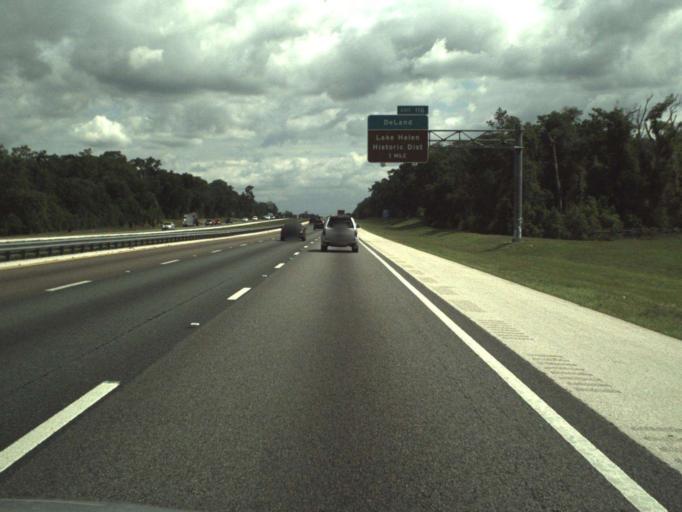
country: US
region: Florida
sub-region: Volusia County
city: Lake Helen
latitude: 28.9689
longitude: -81.2532
